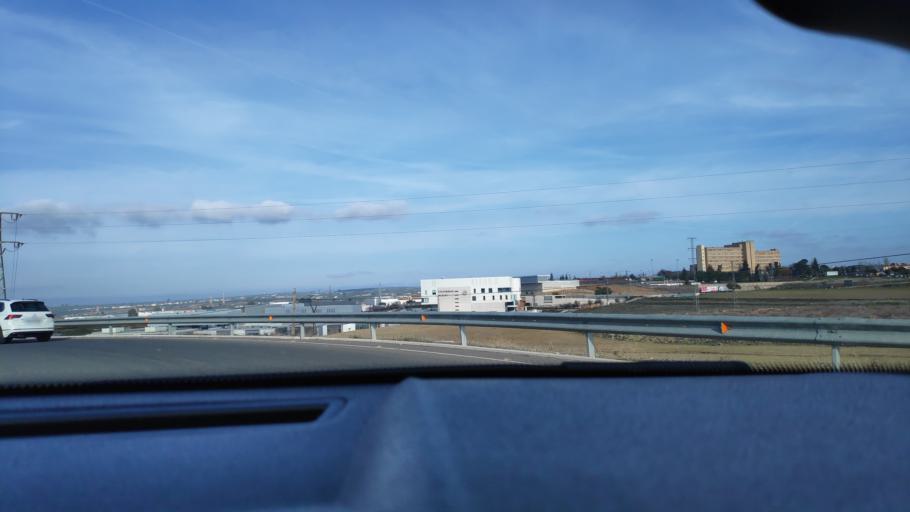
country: ES
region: Andalusia
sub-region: Provincia de Jaen
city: Linares
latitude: 38.0821
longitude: -3.6443
